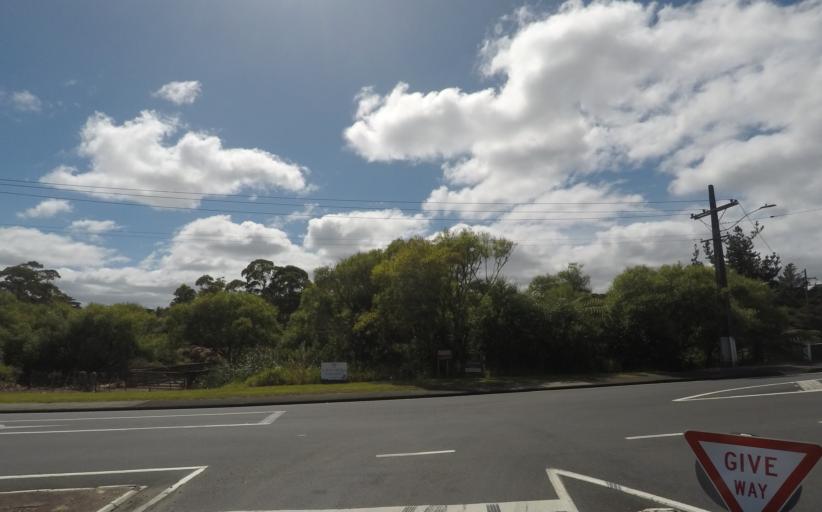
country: NZ
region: Auckland
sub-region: Auckland
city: Muriwai Beach
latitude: -36.8504
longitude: 174.5424
